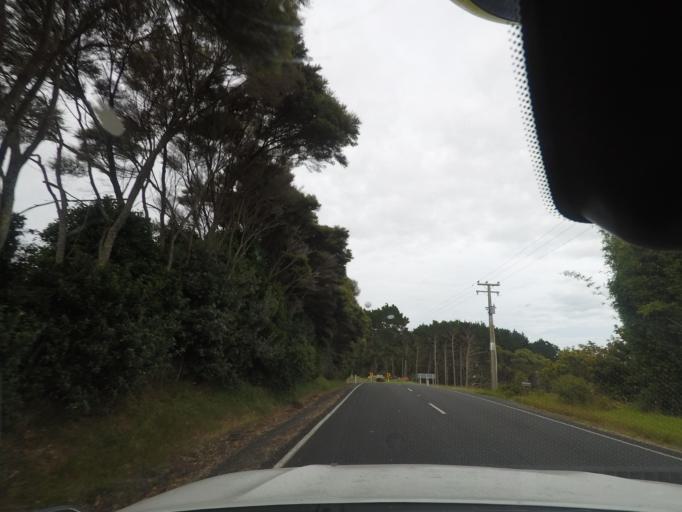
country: NZ
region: Auckland
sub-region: Auckland
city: Parakai
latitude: -36.5180
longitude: 174.2557
